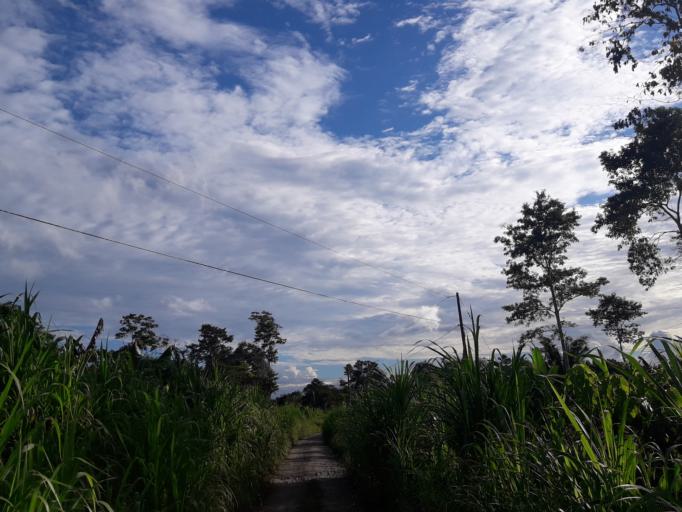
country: EC
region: Orellana
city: Boca Suno
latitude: -0.8870
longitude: -77.3005
